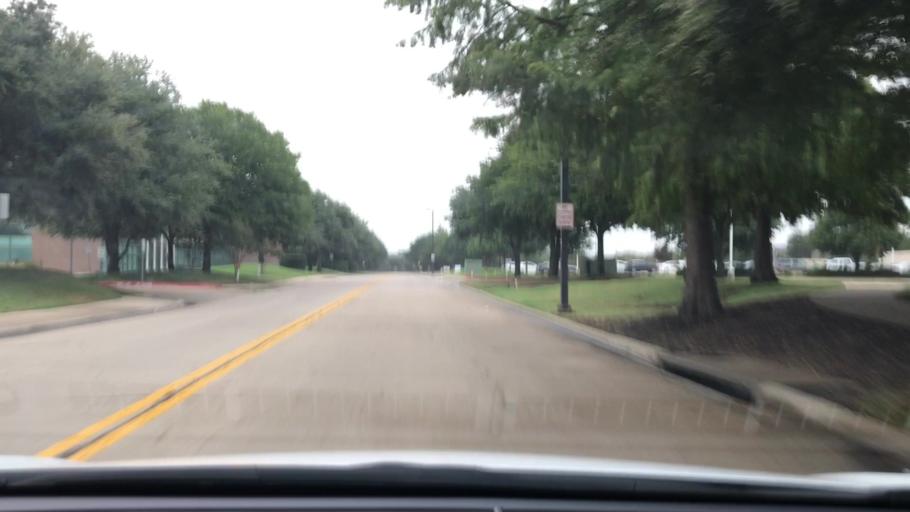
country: US
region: Texas
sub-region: Dallas County
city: Coppell
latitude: 32.9314
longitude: -97.0143
